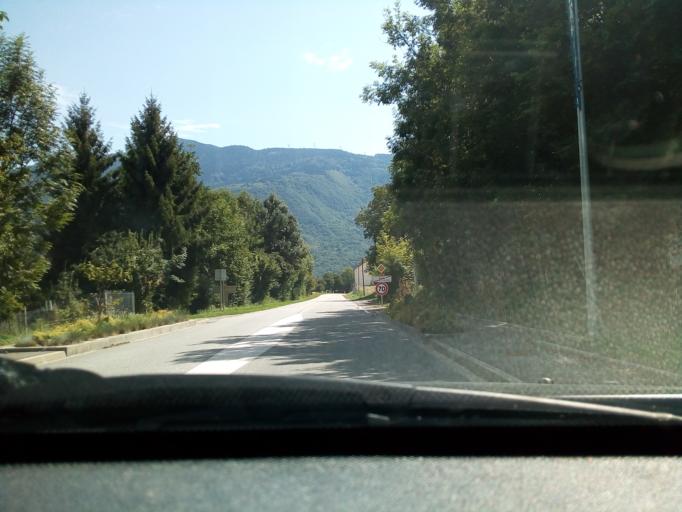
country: FR
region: Rhone-Alpes
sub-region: Departement de l'Isere
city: Brie-et-Angonnes
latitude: 45.1095
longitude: 5.7887
